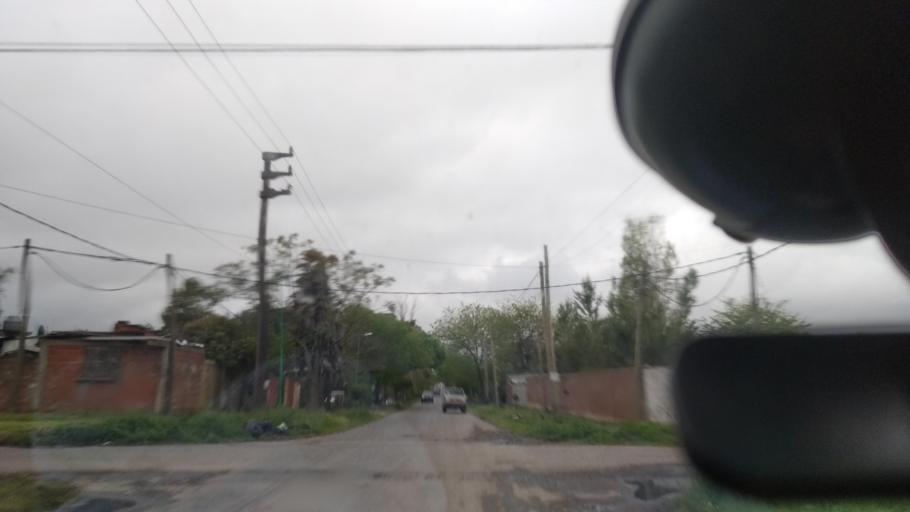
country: AR
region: Buenos Aires
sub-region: Partido de La Plata
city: La Plata
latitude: -34.9521
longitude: -57.9924
